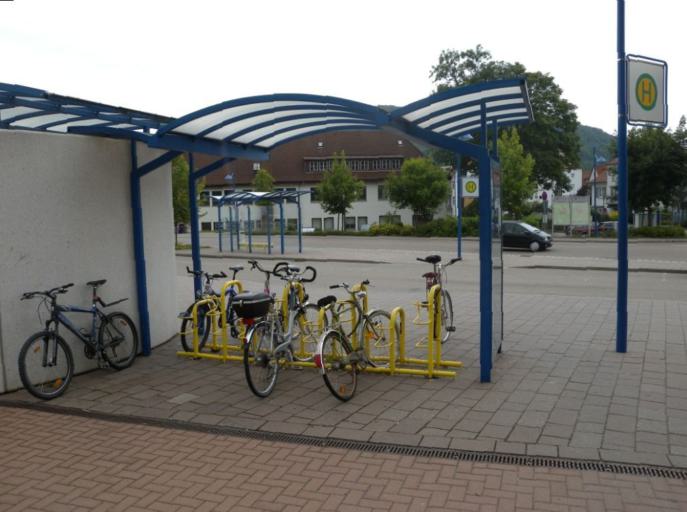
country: DE
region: Baden-Wuerttemberg
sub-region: Regierungsbezirk Stuttgart
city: Oberkochen
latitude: 48.7823
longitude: 10.1072
